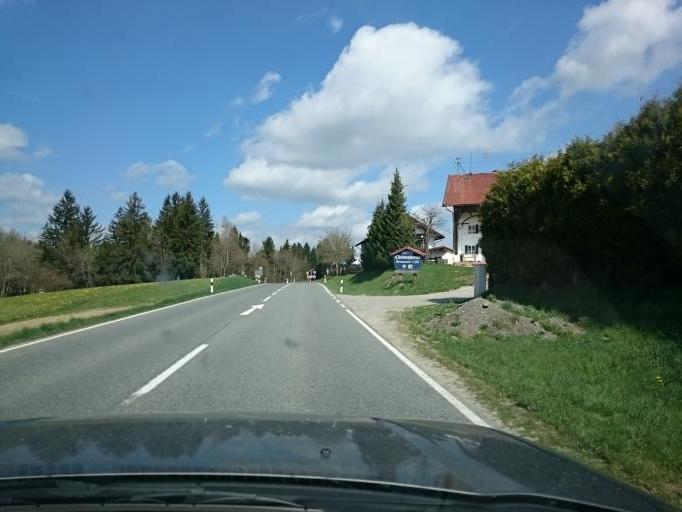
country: DE
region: Bavaria
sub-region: Upper Bavaria
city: Rottenbuch
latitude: 47.7089
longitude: 10.9797
